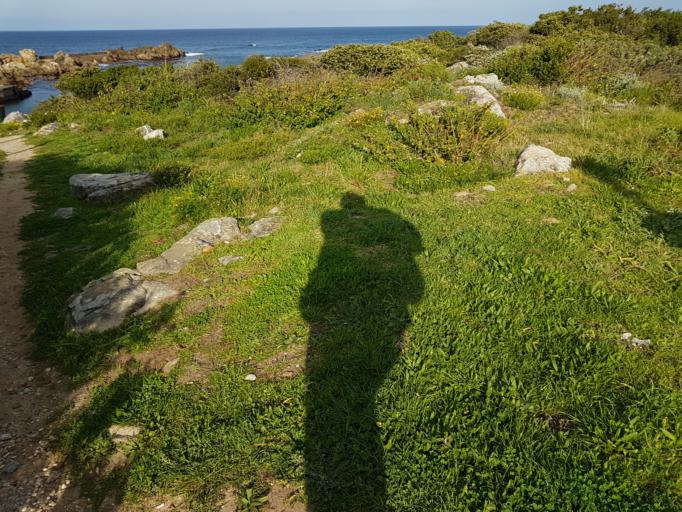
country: ZA
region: Western Cape
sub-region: Overberg District Municipality
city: Grabouw
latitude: -34.3451
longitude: 19.0134
